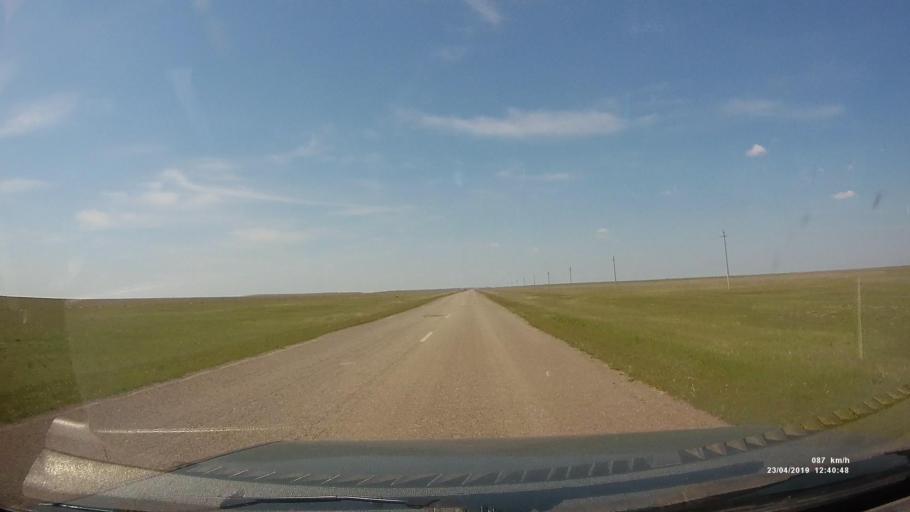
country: RU
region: Kalmykiya
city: Yashalta
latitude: 46.4432
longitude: 42.6909
